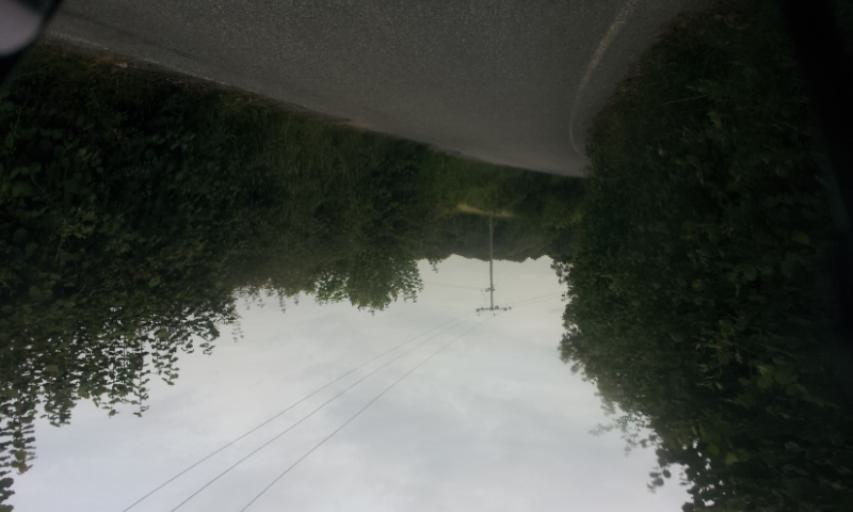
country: GB
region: England
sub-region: Kent
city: Tonbridge
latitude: 51.1729
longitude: 0.2752
